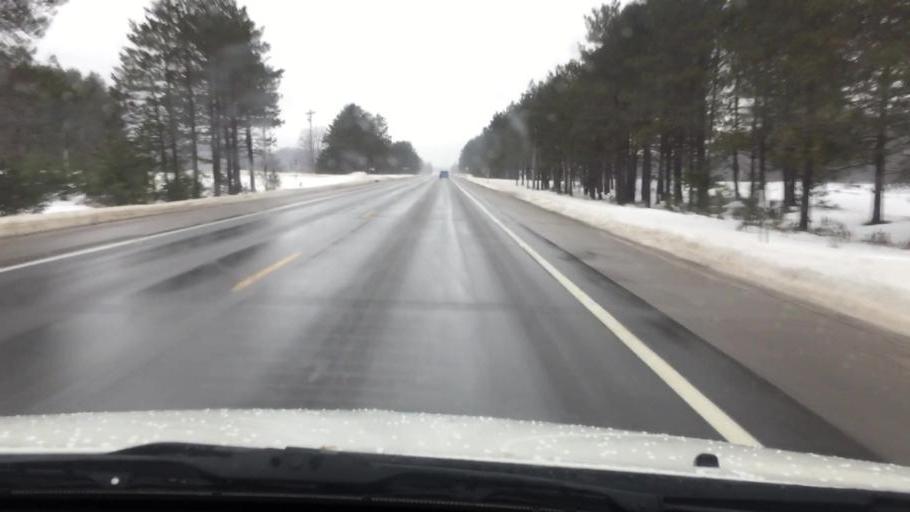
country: US
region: Michigan
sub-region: Kalkaska County
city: Kalkaska
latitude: 44.6859
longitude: -85.2215
